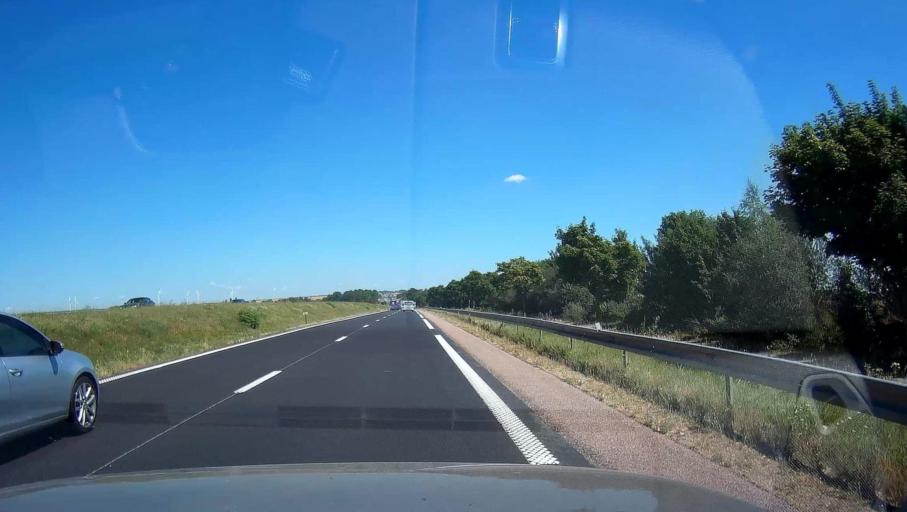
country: FR
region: Champagne-Ardenne
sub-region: Departement de la Marne
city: Warmeriville
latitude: 49.4075
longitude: 4.2533
